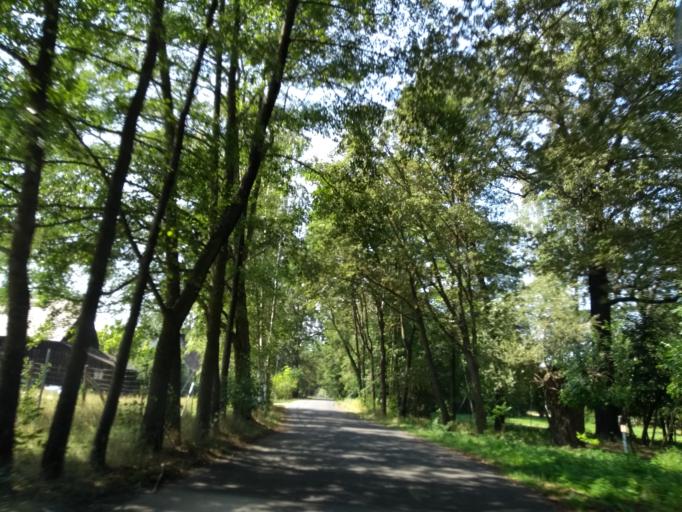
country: DE
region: Brandenburg
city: Burg
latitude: 51.8515
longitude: 14.1217
